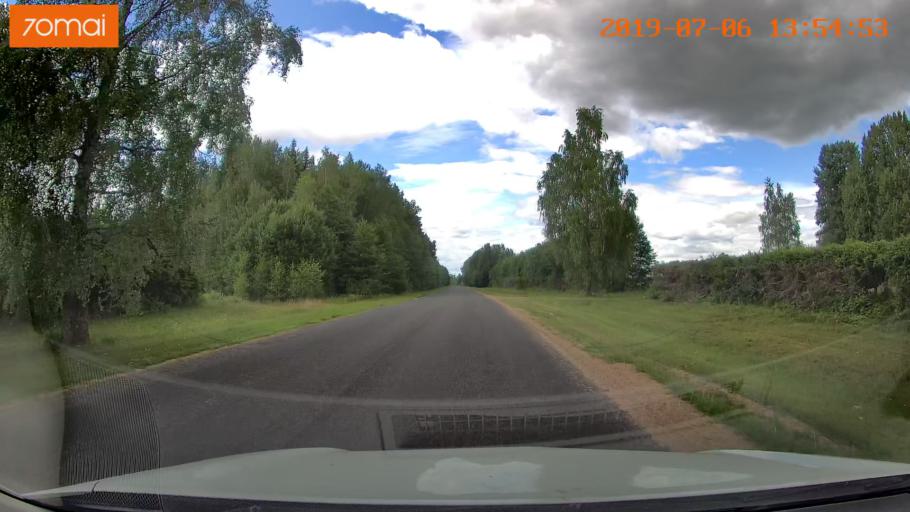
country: BY
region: Minsk
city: Ivyanyets
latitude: 53.7502
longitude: 26.8153
